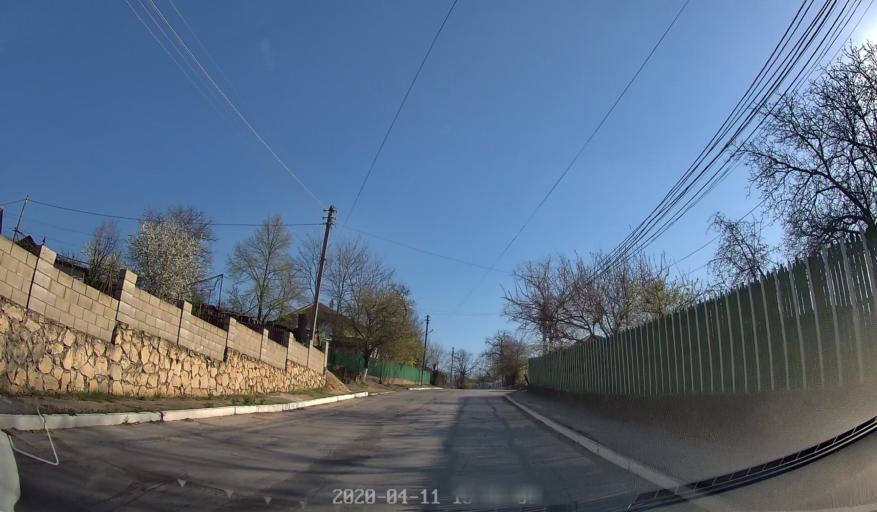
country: MD
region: Chisinau
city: Vadul lui Voda
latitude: 47.0971
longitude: 29.1773
